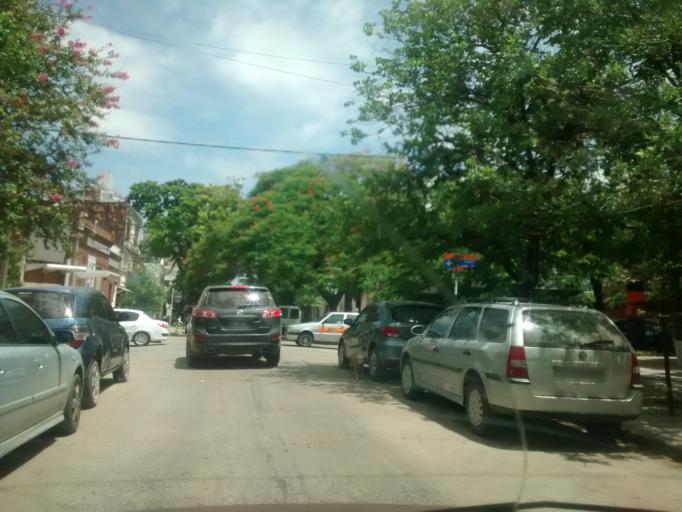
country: AR
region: Chaco
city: Resistencia
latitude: -27.4481
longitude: -58.9793
